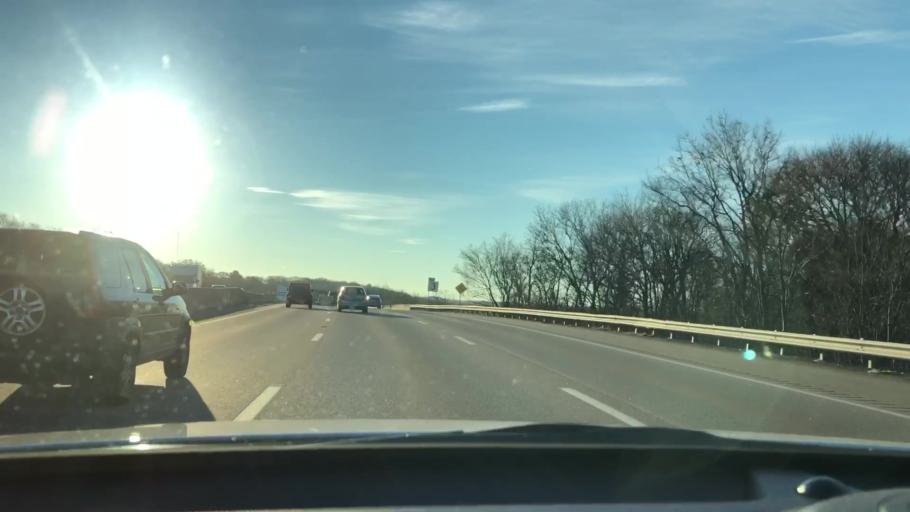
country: US
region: Massachusetts
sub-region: Norfolk County
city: Braintree
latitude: 42.2199
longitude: -71.0009
